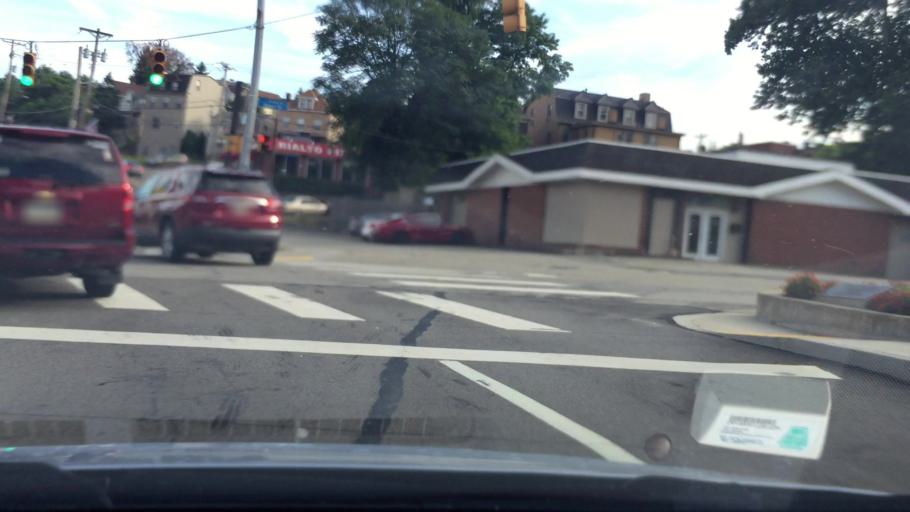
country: US
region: Pennsylvania
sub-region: Allegheny County
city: Homestead
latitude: 40.4272
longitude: -79.9386
